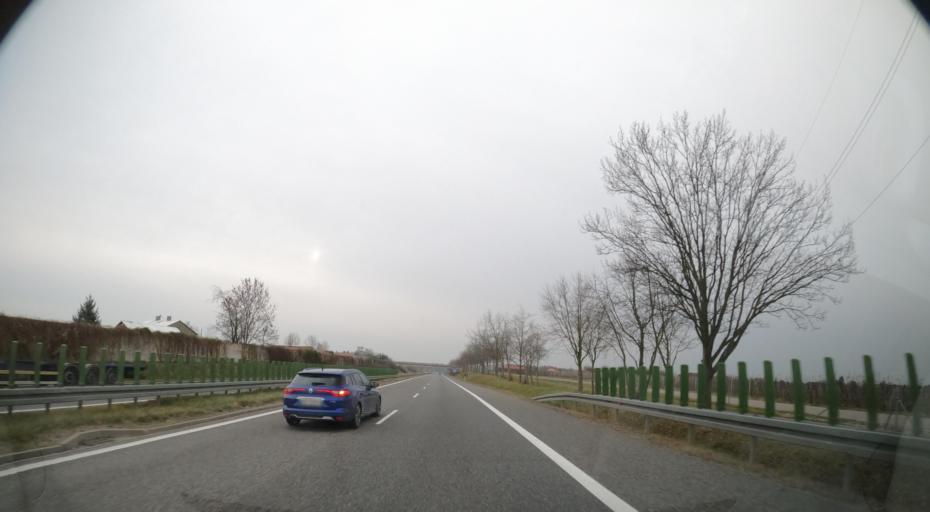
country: PL
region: Masovian Voivodeship
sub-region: Powiat grojecki
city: Grojec
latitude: 51.8886
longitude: 20.8560
